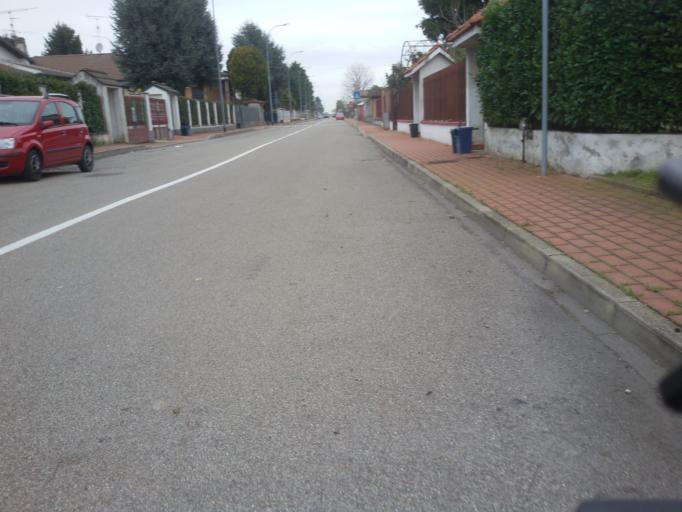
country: IT
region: Lombardy
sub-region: Citta metropolitana di Milano
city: Noviglio
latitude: 45.3569
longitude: 9.0527
